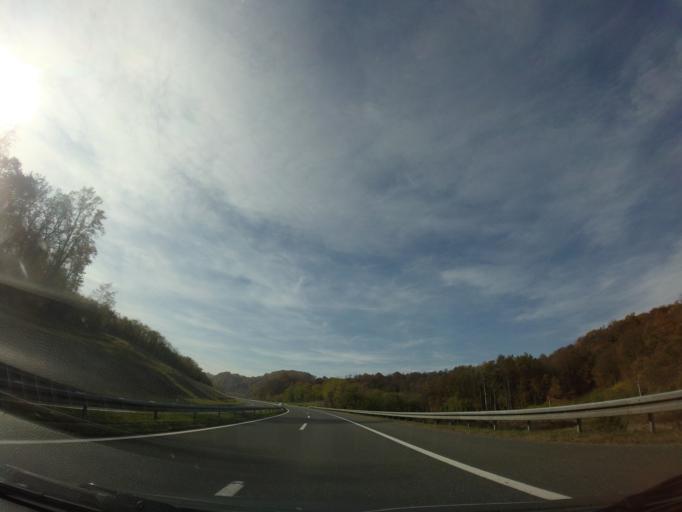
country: HR
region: Varazdinska
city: Remetinec
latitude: 46.1268
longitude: 16.3128
